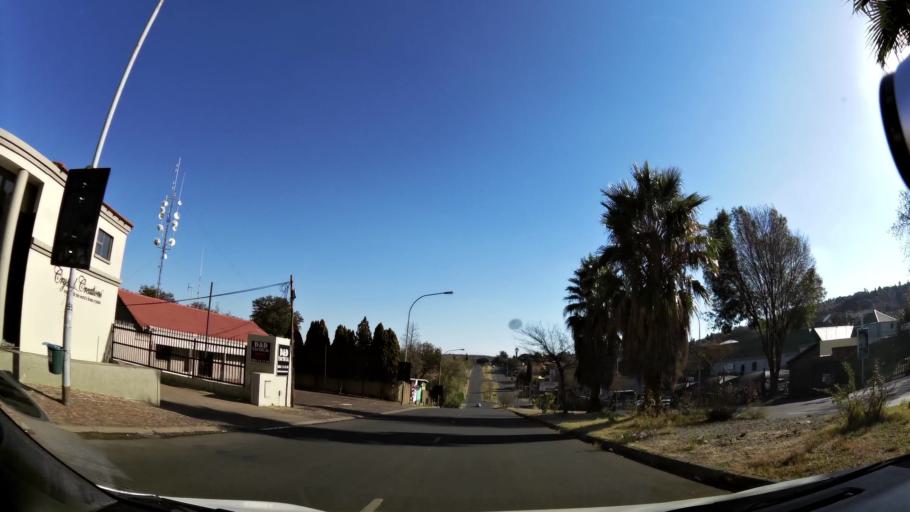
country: ZA
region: Gauteng
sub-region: City of Johannesburg Metropolitan Municipality
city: Johannesburg
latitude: -26.2868
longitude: 28.0544
